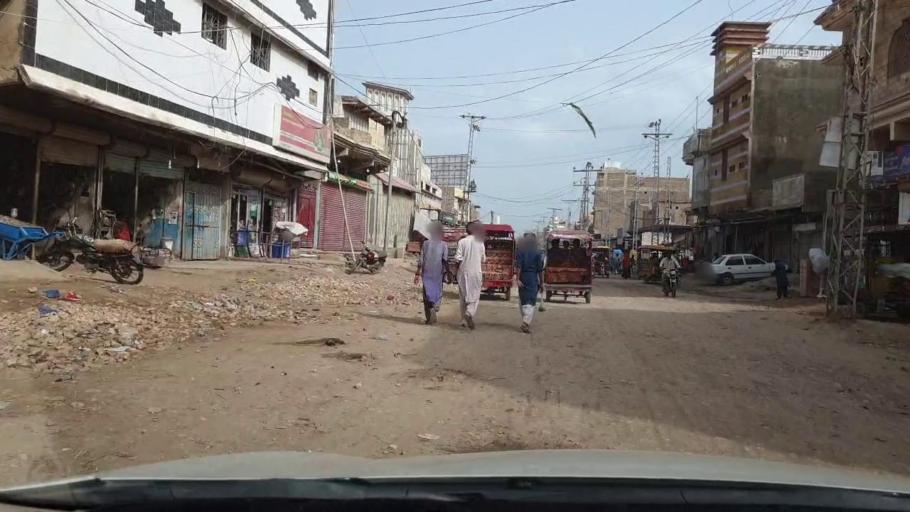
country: PK
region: Sindh
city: Matli
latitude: 25.0413
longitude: 68.6606
